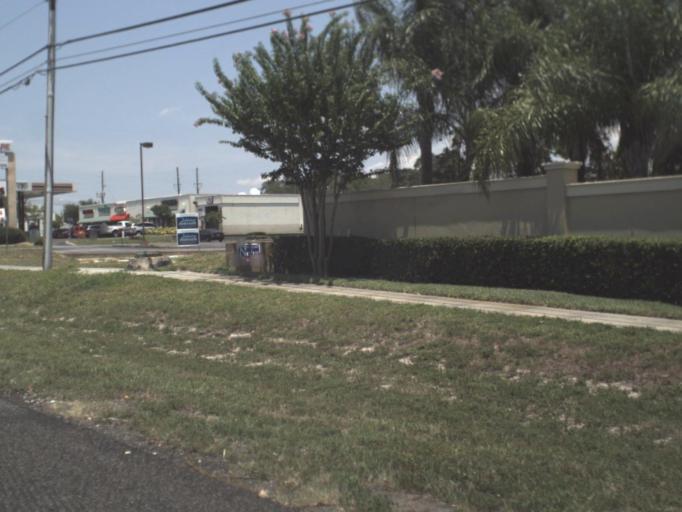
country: US
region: Florida
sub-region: Pinellas County
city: Tarpon Springs
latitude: 28.1215
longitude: -82.7398
